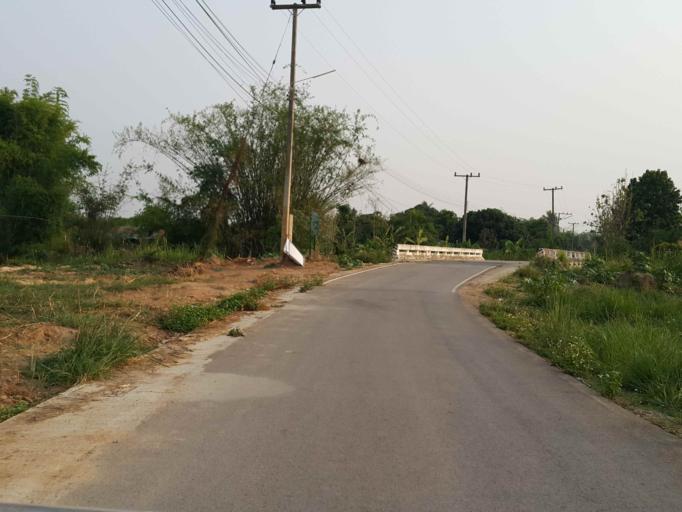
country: TH
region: Chiang Mai
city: Mae Taeng
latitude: 18.9969
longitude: 98.9836
